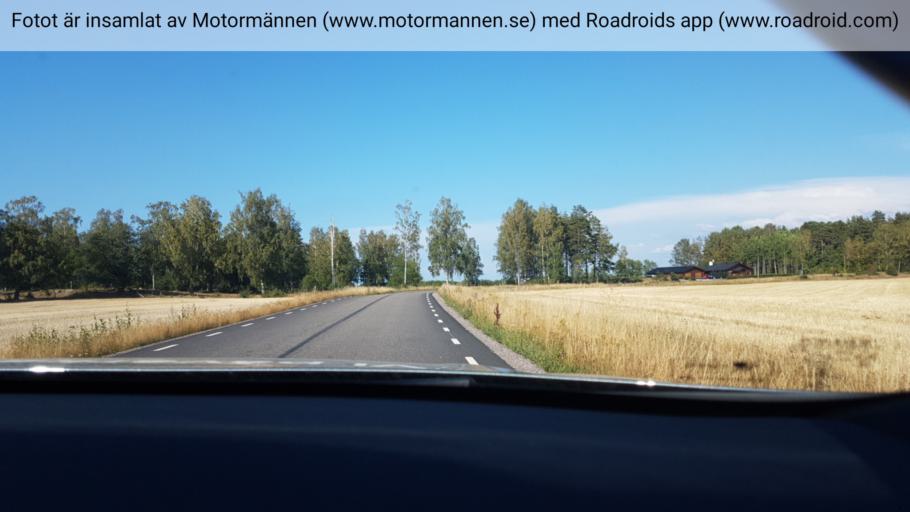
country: SE
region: Vaestra Goetaland
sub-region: Mariestads Kommun
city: Mariestad
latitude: 58.6402
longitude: 13.6767
